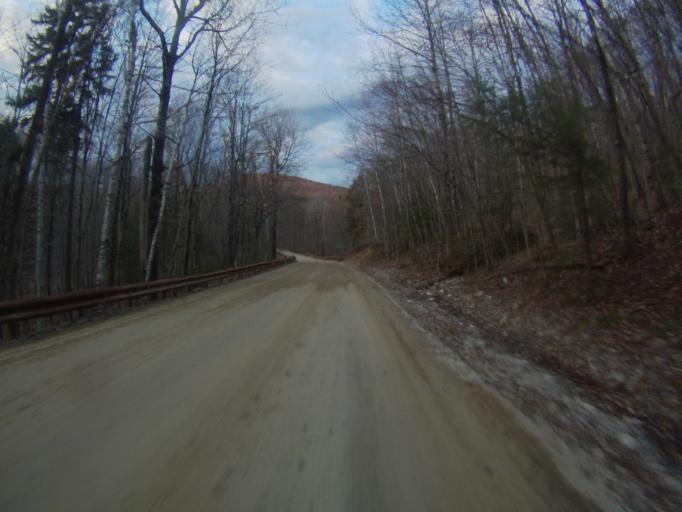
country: US
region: Vermont
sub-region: Rutland County
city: Brandon
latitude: 43.9148
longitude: -73.0180
